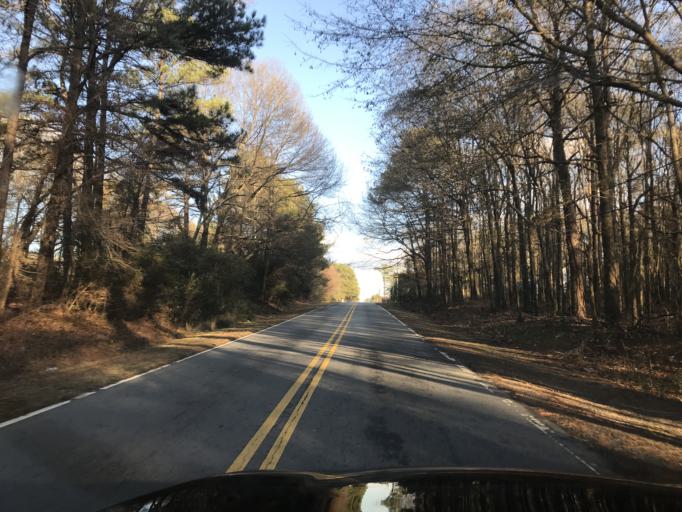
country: US
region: Georgia
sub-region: Fulton County
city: College Park
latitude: 33.6230
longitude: -84.4847
